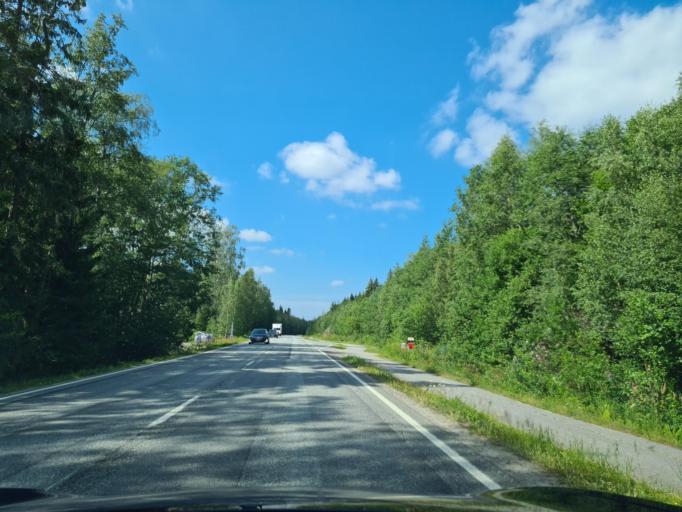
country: FI
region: Ostrobothnia
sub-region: Vaasa
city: Vaasa
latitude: 63.1978
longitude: 21.5412
